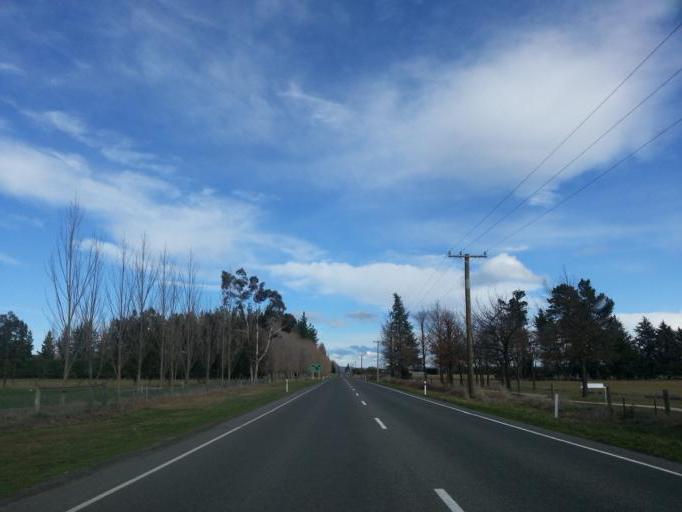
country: NZ
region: Canterbury
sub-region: Hurunui District
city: Amberley
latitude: -42.7769
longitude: 172.8459
